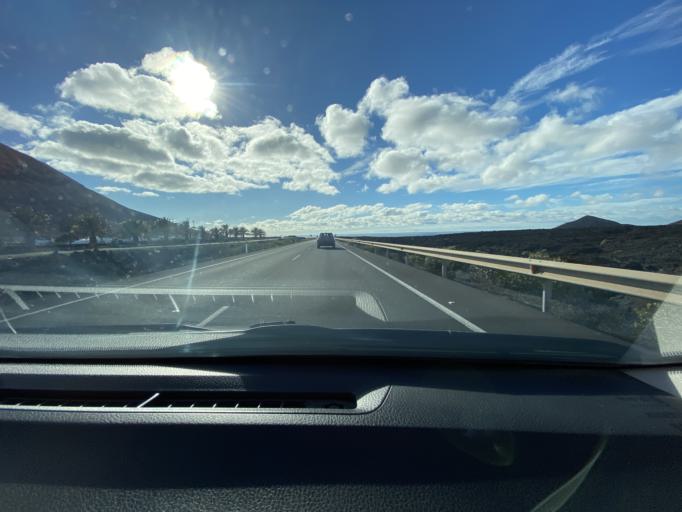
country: ES
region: Canary Islands
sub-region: Provincia de Las Palmas
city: Yaiza
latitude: 28.9575
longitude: -13.7747
